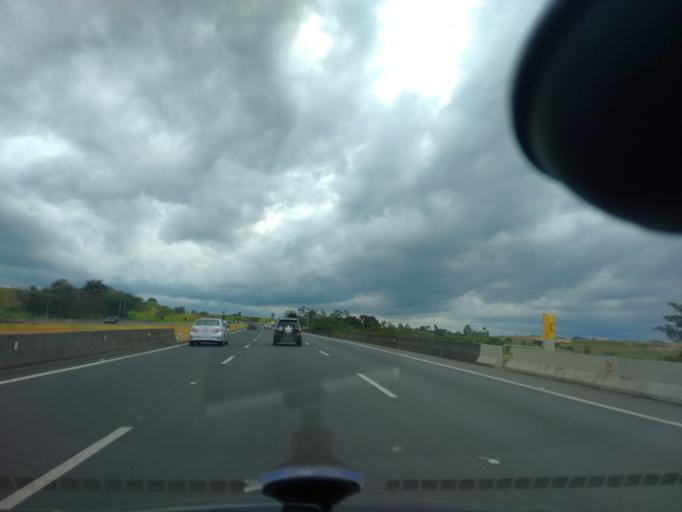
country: BR
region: Sao Paulo
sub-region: Campinas
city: Campinas
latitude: -22.9208
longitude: -47.1381
